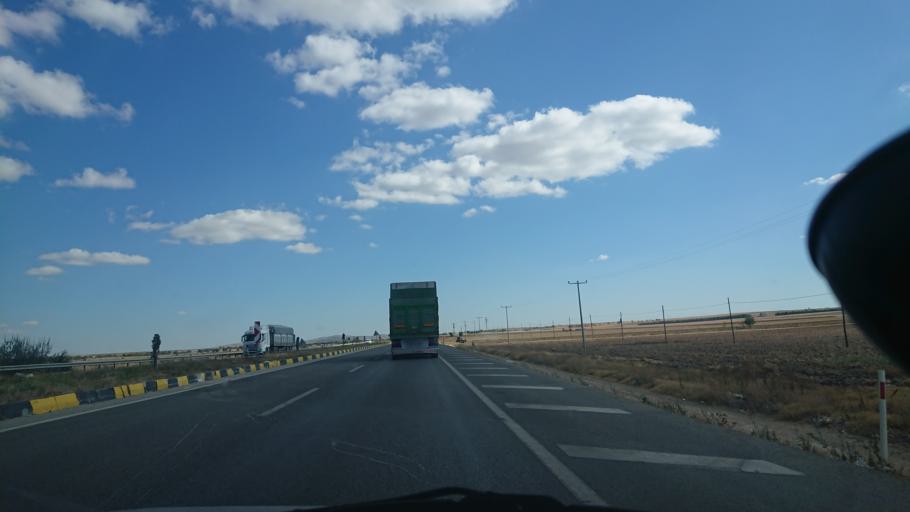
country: TR
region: Eskisehir
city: Mahmudiye
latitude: 39.5543
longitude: 30.9228
